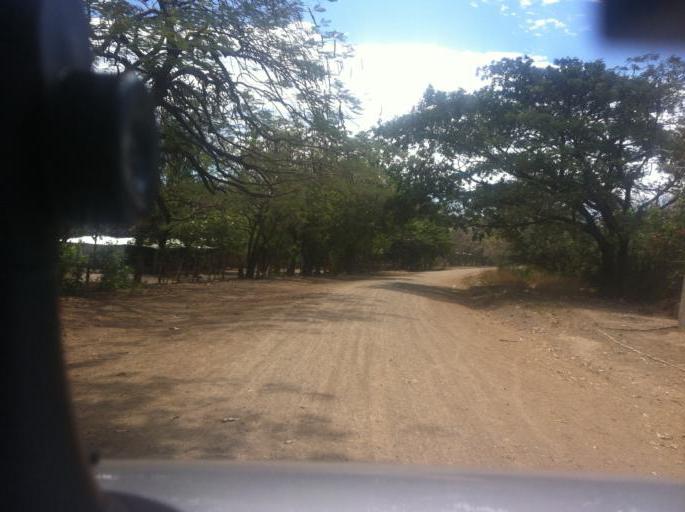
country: NI
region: Granada
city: Nandaime
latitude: 11.6231
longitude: -86.0249
